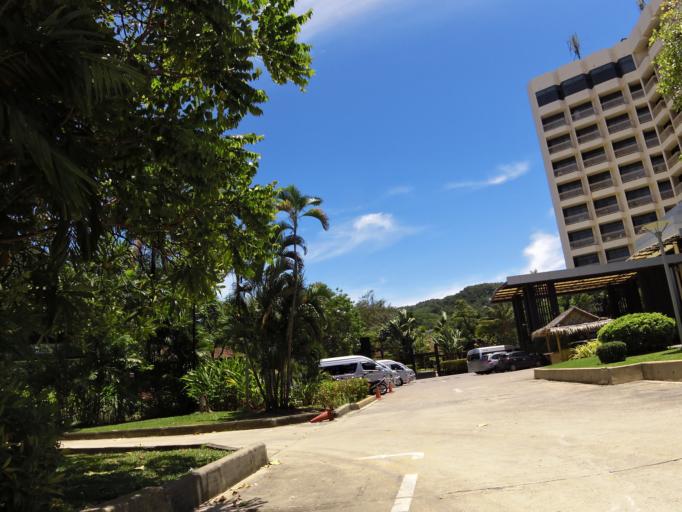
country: TH
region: Phuket
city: Ban Karon
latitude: 7.8497
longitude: 98.2953
